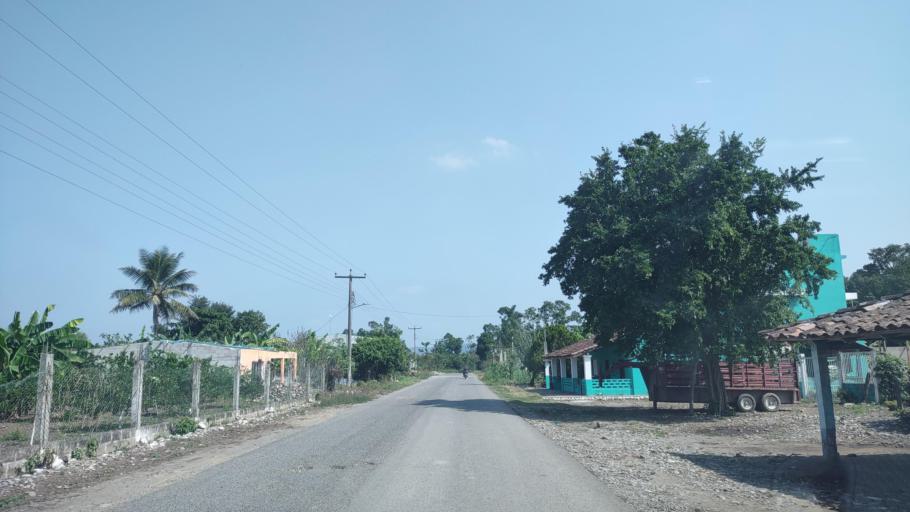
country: MX
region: Puebla
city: Espinal
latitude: 20.2554
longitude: -97.3291
